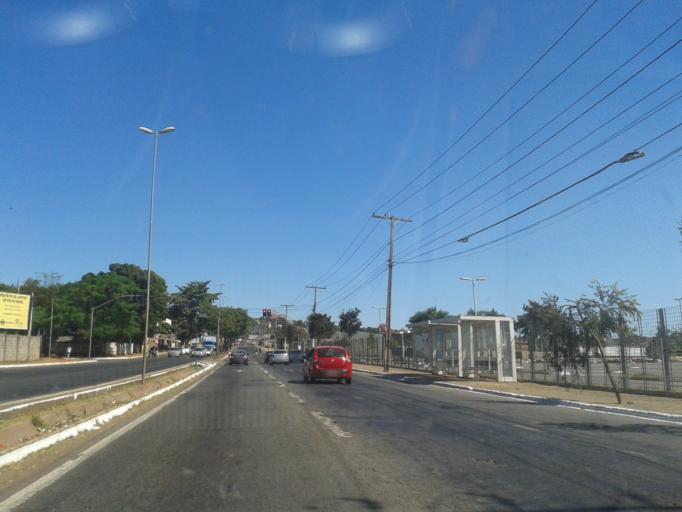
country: BR
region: Goias
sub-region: Goiania
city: Goiania
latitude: -16.6322
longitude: -49.2790
